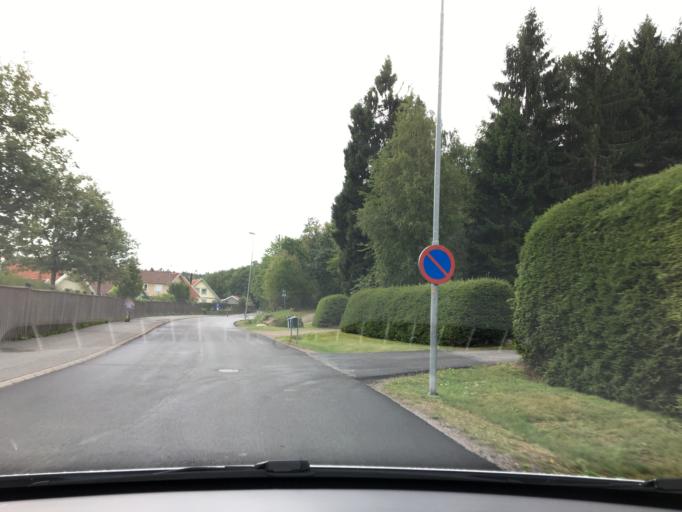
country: SE
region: Vaestra Goetaland
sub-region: Ale Kommun
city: Nodinge-Nol
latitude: 57.8864
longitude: 12.0466
